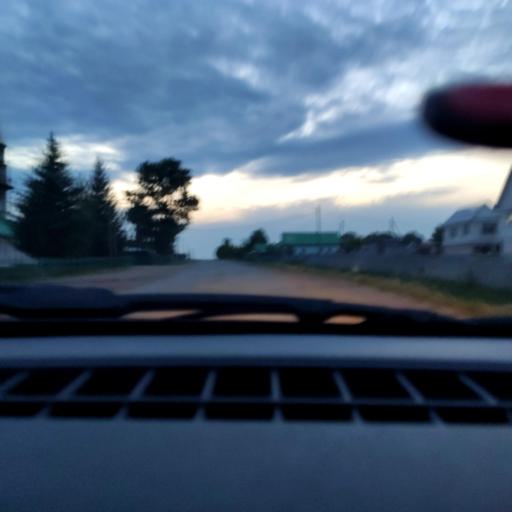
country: RU
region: Bashkortostan
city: Tolbazy
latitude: 54.2924
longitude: 55.8131
